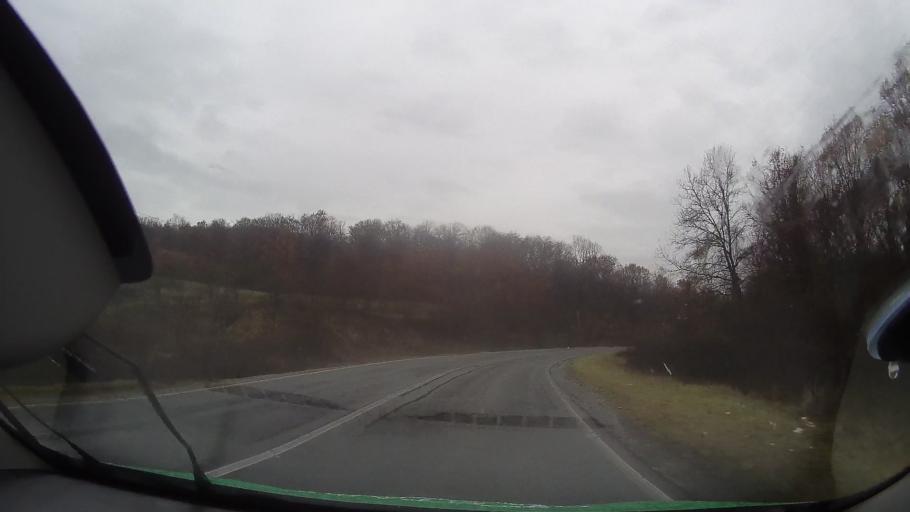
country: RO
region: Bihor
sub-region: Comuna Rabagani
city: Rabagani
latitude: 46.7326
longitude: 22.2308
